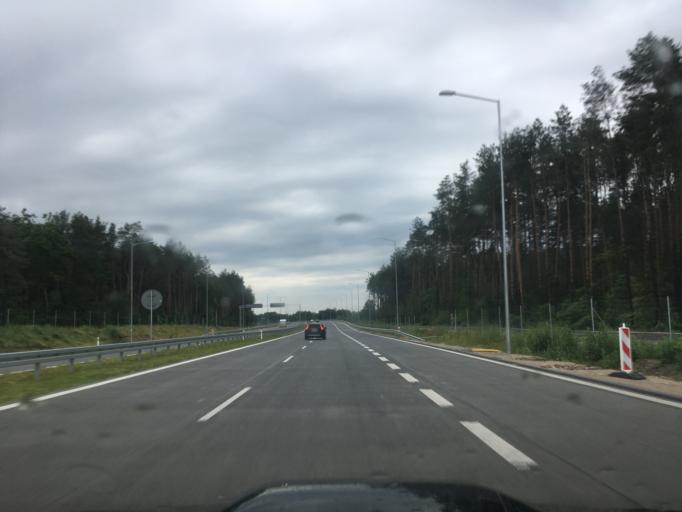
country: PL
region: Masovian Voivodeship
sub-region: Powiat piaseczynski
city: Gora Kalwaria
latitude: 51.9732
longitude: 21.1923
